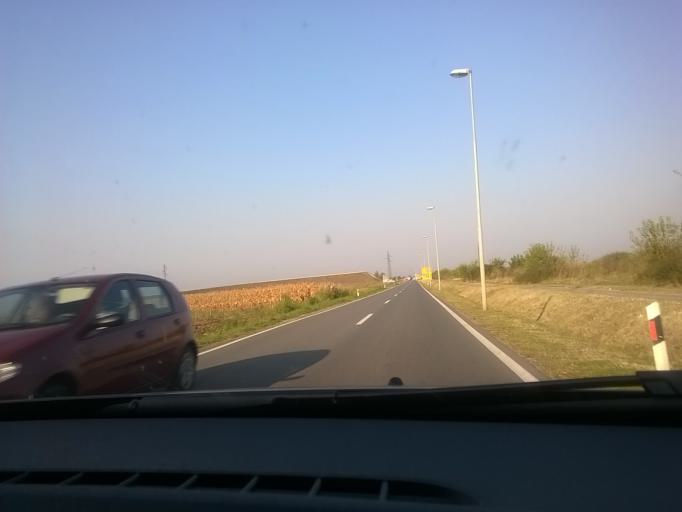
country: RS
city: Pavlis
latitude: 45.1124
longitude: 21.2668
